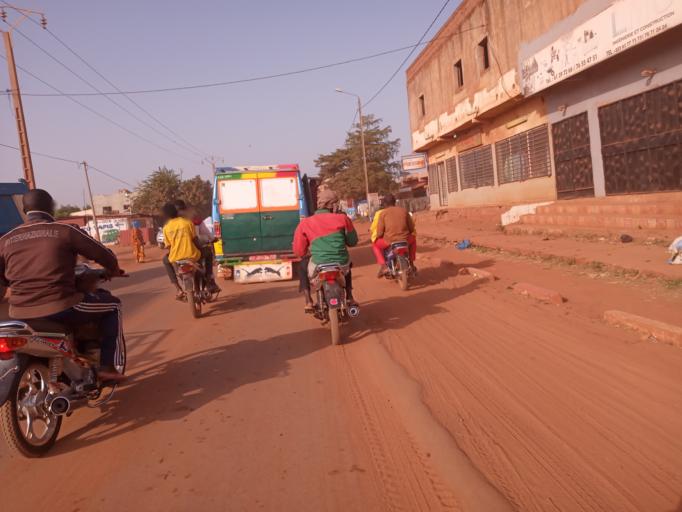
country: ML
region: Bamako
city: Bamako
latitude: 12.5793
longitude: -8.0253
